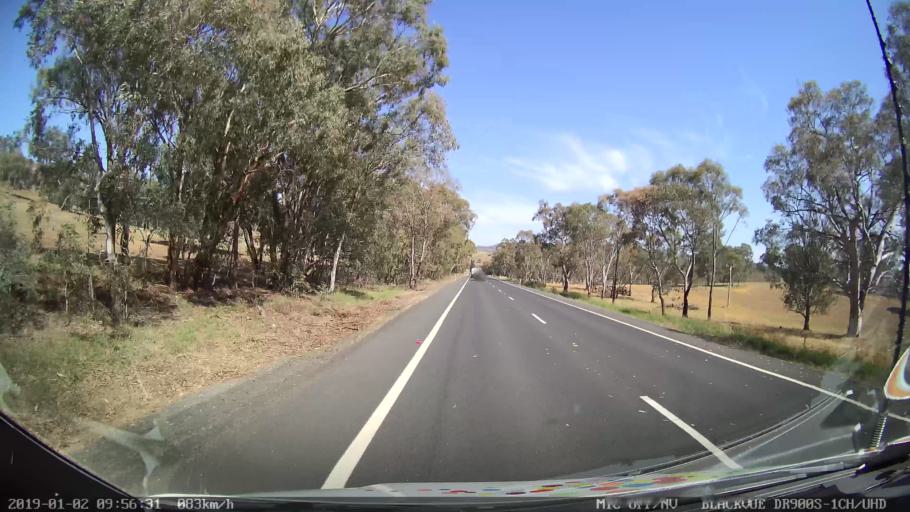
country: AU
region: New South Wales
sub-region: Tumut Shire
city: Tumut
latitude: -35.2145
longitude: 148.1757
